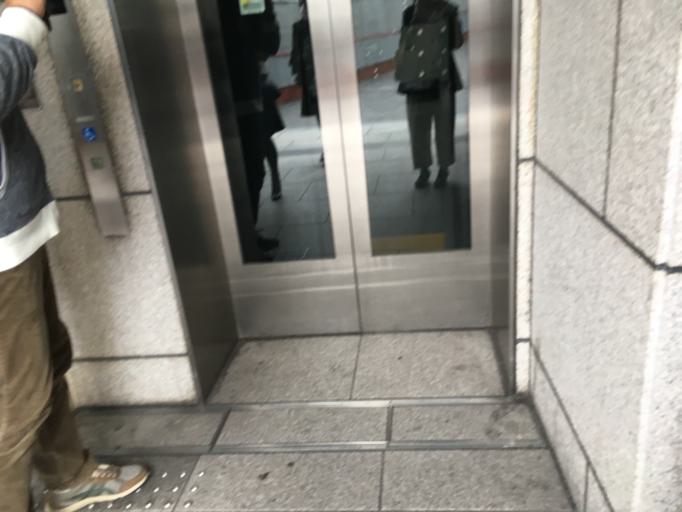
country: JP
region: Osaka
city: Osaka-shi
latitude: 34.7021
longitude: 135.4981
